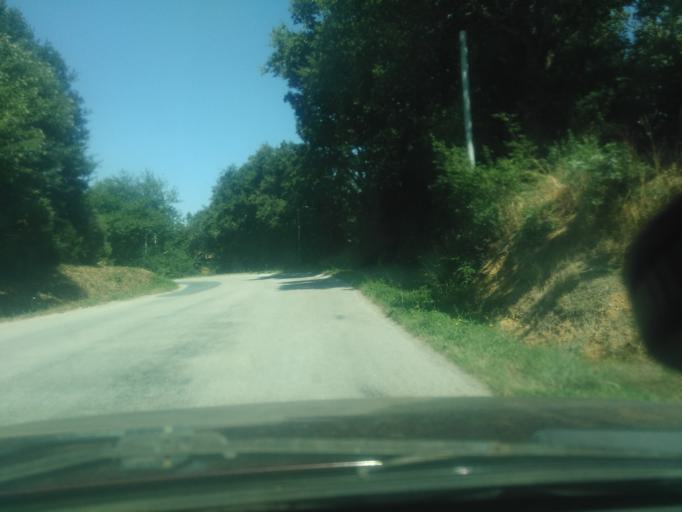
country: FR
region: Pays de la Loire
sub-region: Departement de la Vendee
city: Dompierre-sur-Yon
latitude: 46.7164
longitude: -1.3970
